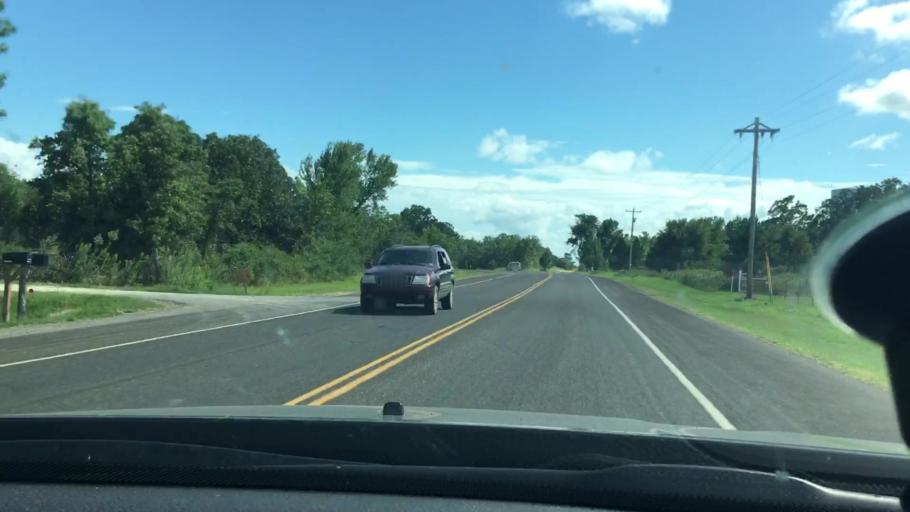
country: US
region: Oklahoma
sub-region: Sequoyah County
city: Vian
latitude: 35.5687
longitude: -94.9853
